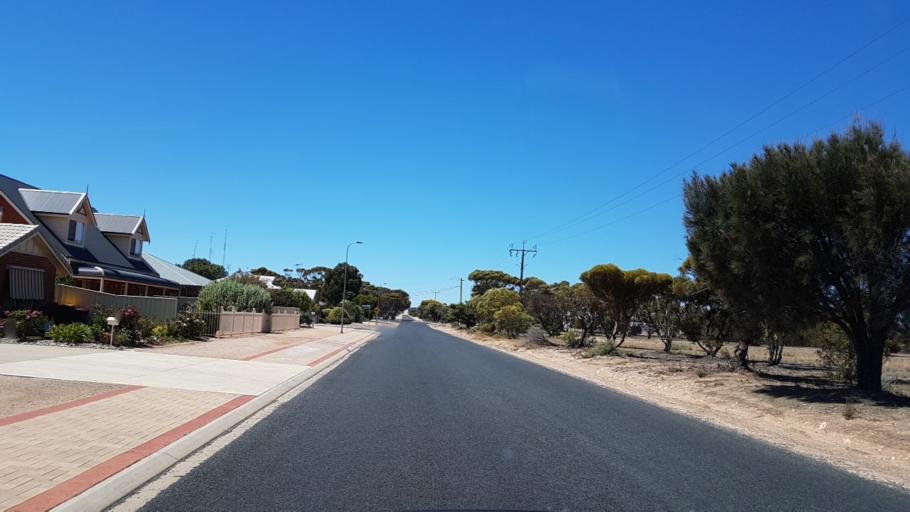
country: AU
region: South Australia
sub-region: Copper Coast
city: Wallaroo
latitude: -34.0626
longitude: 137.5917
